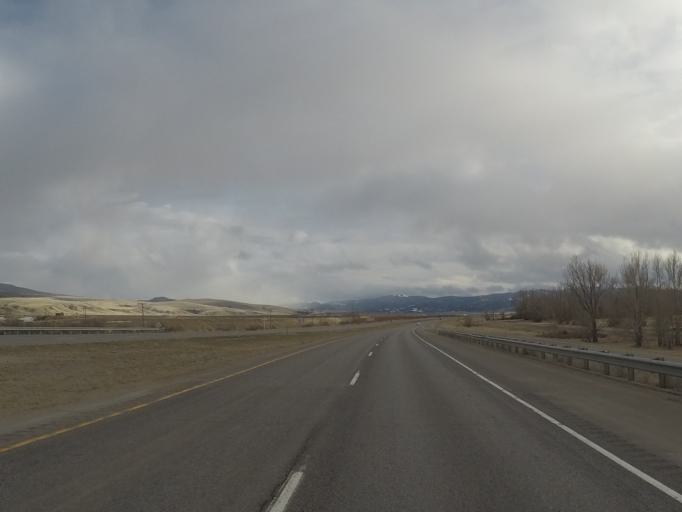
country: US
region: Montana
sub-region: Deer Lodge County
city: Warm Springs
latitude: 46.1811
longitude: -112.7840
